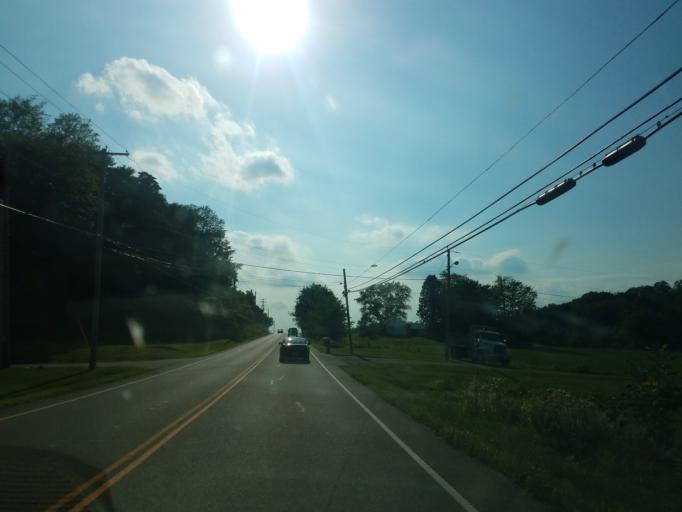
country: US
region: Ohio
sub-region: Stark County
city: Canal Fulton
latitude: 40.8815
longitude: -81.5540
